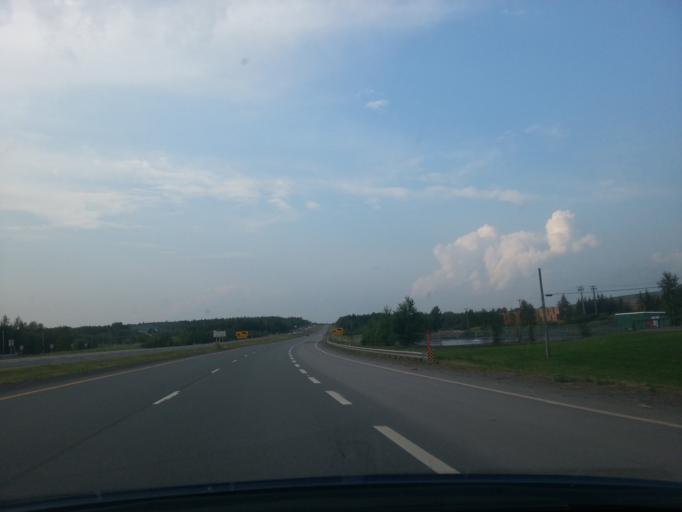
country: CA
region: New Brunswick
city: Harrison Brook
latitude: 47.1898
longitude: -67.9330
